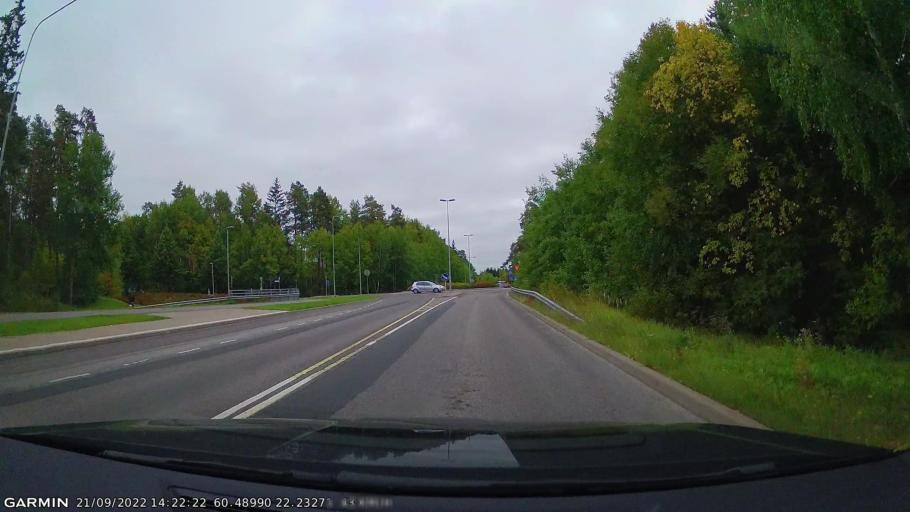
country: FI
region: Varsinais-Suomi
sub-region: Turku
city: Rusko
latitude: 60.4896
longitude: 22.2327
